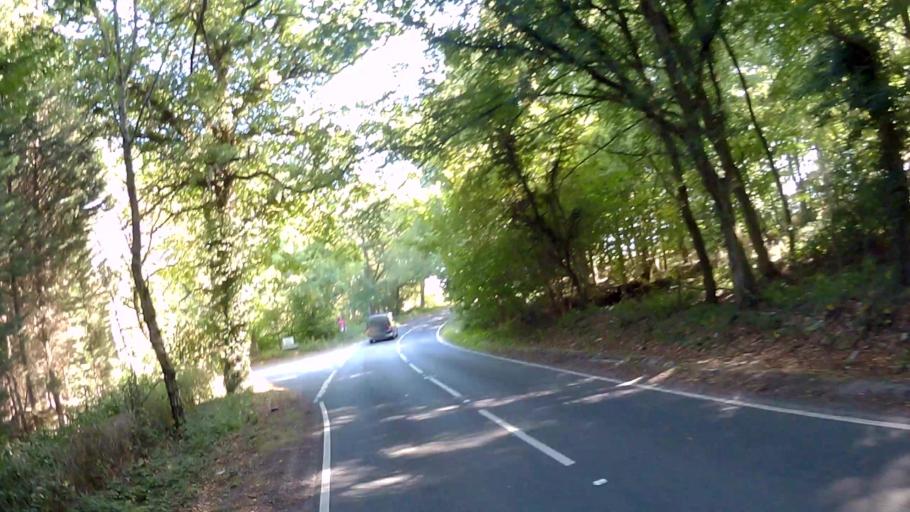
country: GB
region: England
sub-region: Surrey
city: Farnham
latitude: 51.1901
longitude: -0.7638
